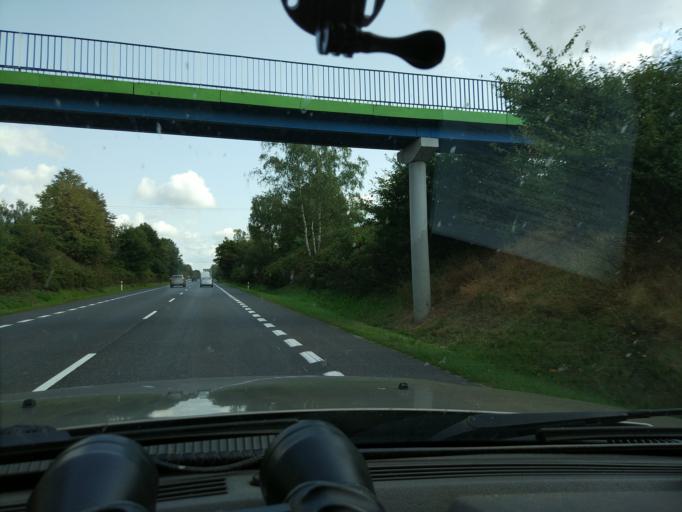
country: PL
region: Masovian Voivodeship
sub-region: Powiat mlawski
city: Mlawa
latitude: 53.0963
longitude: 20.3814
